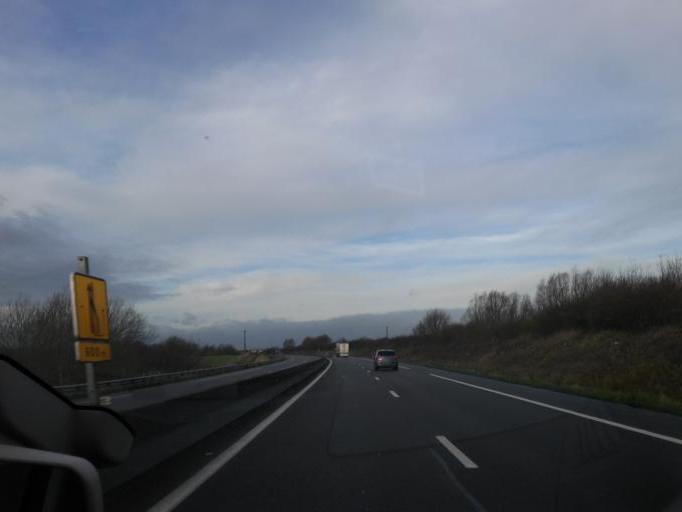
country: FR
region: Picardie
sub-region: Departement de la Somme
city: Chaulnes
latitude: 49.8566
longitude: 2.7896
